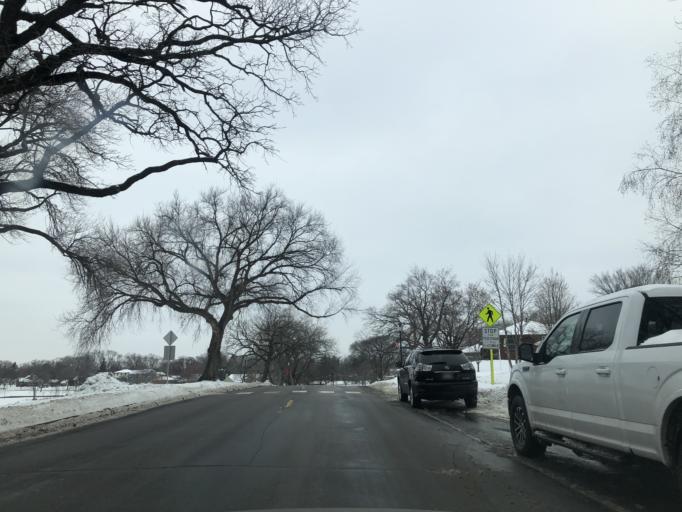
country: US
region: Minnesota
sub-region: Hennepin County
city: Robbinsdale
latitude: 45.0293
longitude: -93.3244
